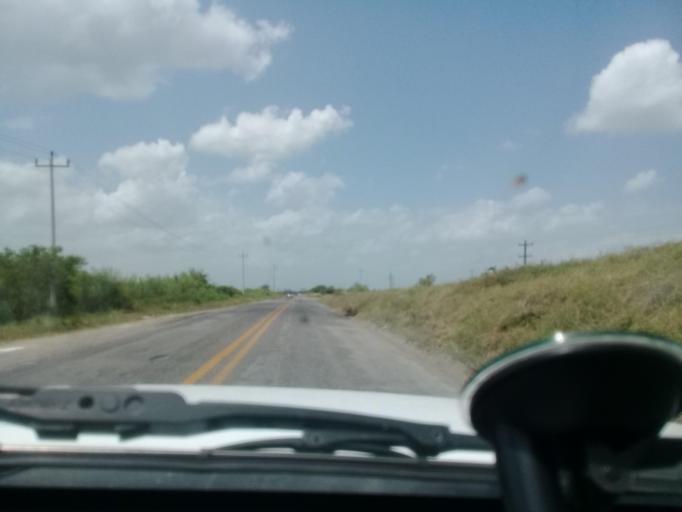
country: MX
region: Veracruz
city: Moralillo
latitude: 22.1814
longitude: -98.0197
